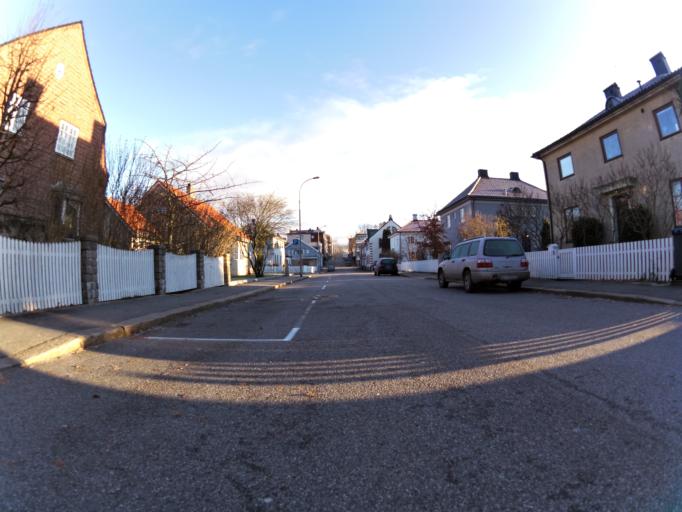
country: NO
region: Ostfold
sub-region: Fredrikstad
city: Fredrikstad
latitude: 59.2090
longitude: 10.9444
